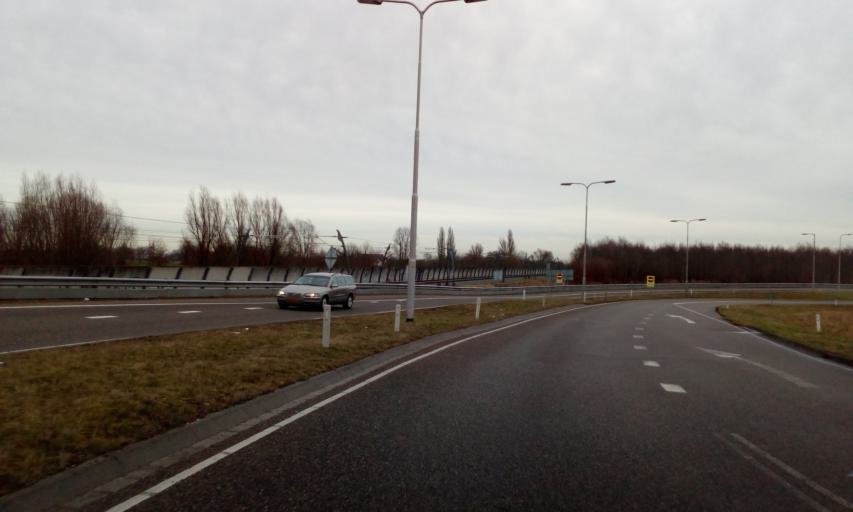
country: NL
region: South Holland
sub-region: Gemeente Gorinchem
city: Gorinchem
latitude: 51.8434
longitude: 4.9375
